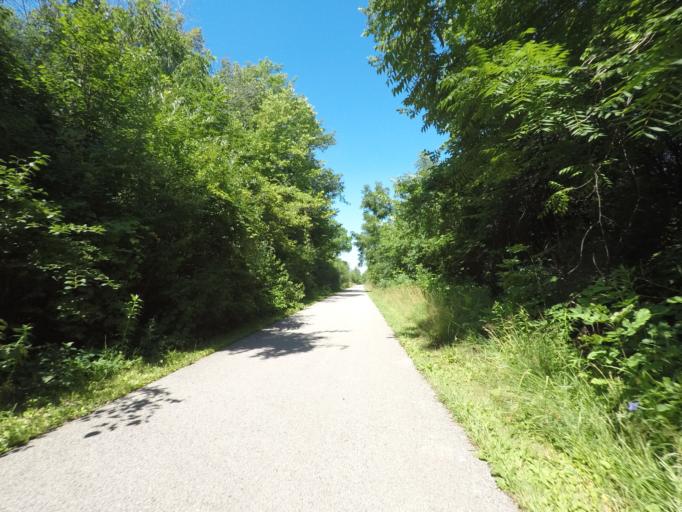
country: US
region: Wisconsin
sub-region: Milwaukee County
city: West Allis
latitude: 43.0246
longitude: -88.0002
